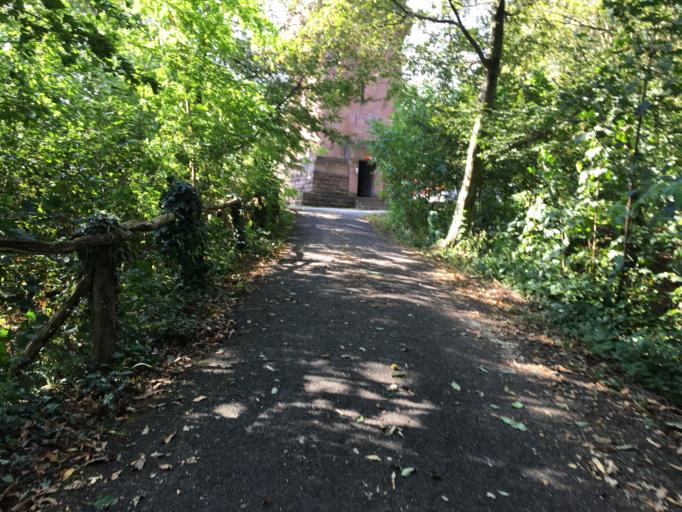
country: DE
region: Baden-Wuerttemberg
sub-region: Karlsruhe Region
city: Heidelberg
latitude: 49.4164
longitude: 8.7003
